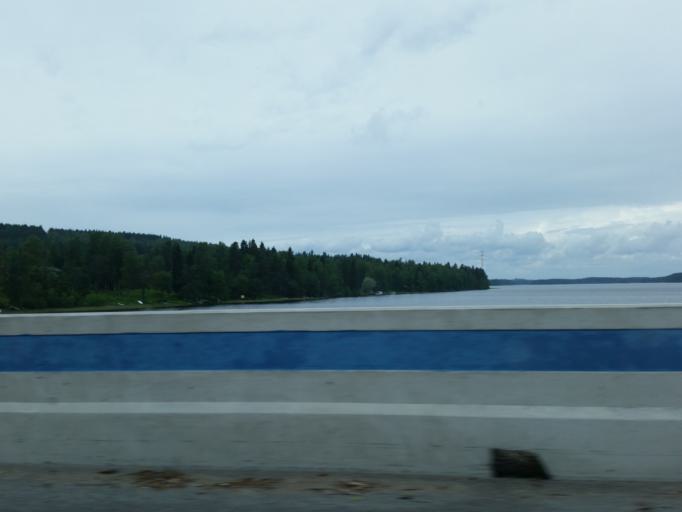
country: FI
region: Northern Savo
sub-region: Kuopio
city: Kuopio
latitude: 62.9391
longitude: 27.6664
